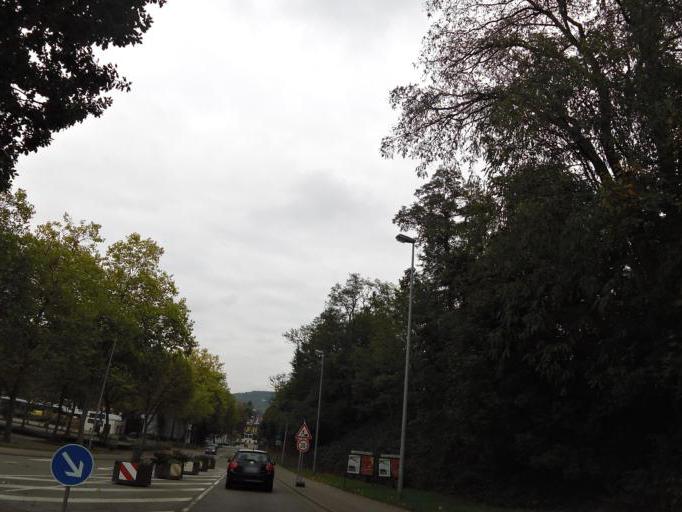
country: DE
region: Saarland
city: Sankt Ingbert
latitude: 49.2786
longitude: 7.1092
